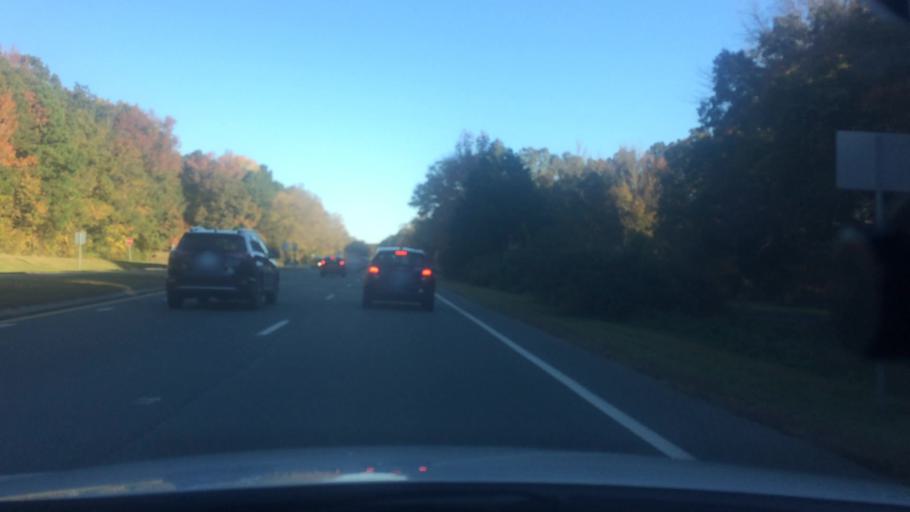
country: US
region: North Carolina
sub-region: Orange County
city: Chapel Hill
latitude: 35.9198
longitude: -79.0259
